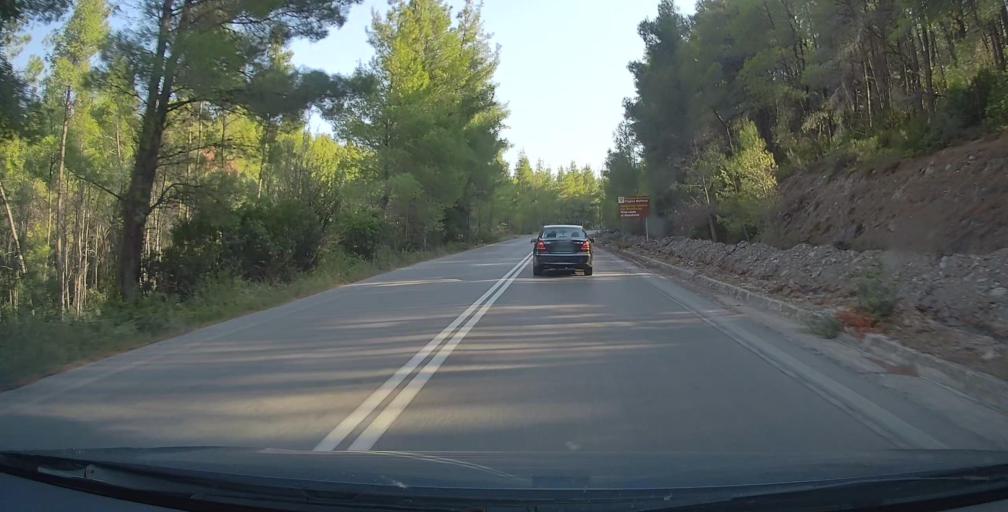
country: GR
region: Central Macedonia
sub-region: Nomos Chalkidikis
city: Neos Marmaras
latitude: 40.0745
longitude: 23.8062
